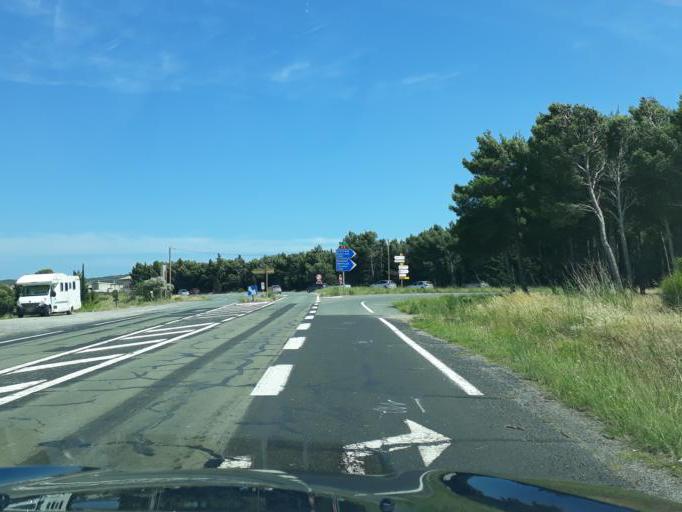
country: FR
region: Languedoc-Roussillon
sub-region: Departement de l'Aude
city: Sigean
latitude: 43.0336
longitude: 2.9583
